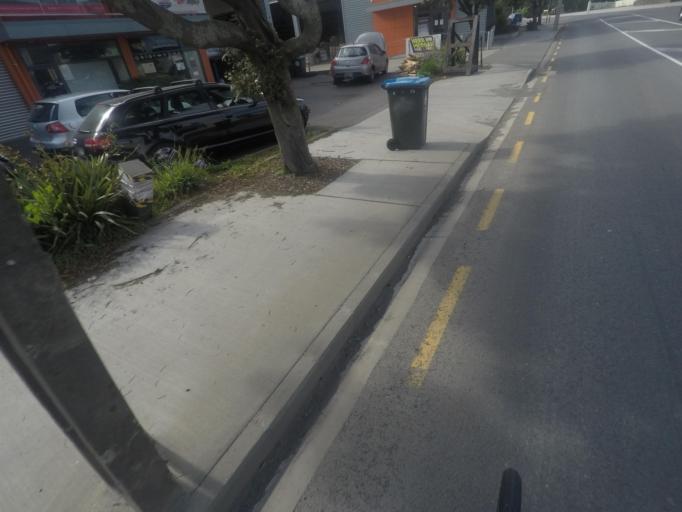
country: NZ
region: Auckland
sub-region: Auckland
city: Mangere
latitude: -36.9275
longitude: 174.7861
